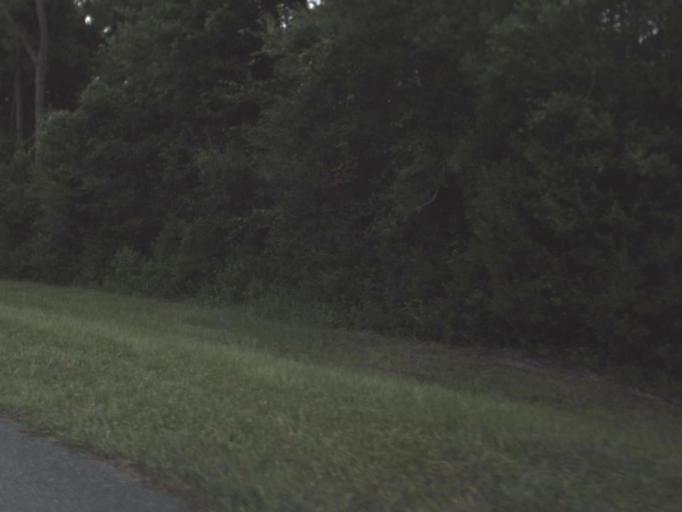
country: US
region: Florida
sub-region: Baker County
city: Macclenny
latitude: 30.1321
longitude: -82.1970
